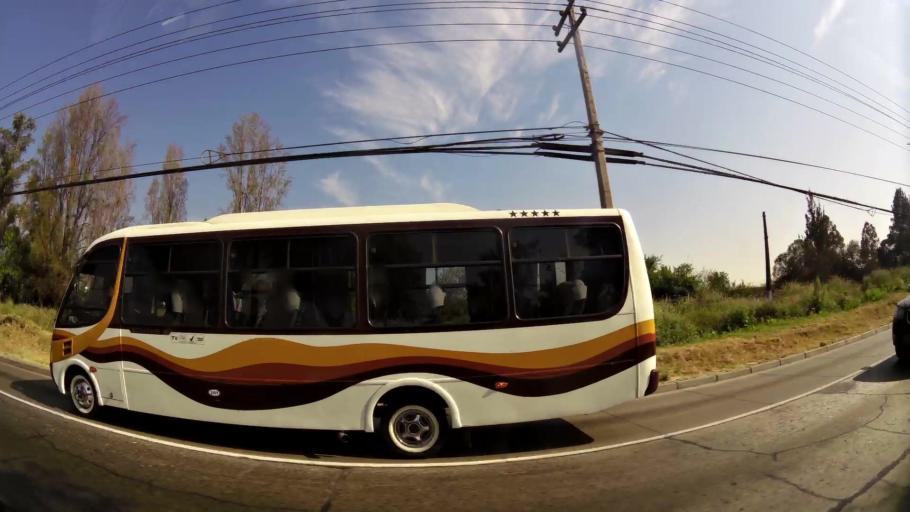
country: CL
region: Santiago Metropolitan
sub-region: Provincia de Maipo
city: San Bernardo
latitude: -33.5416
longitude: -70.7779
